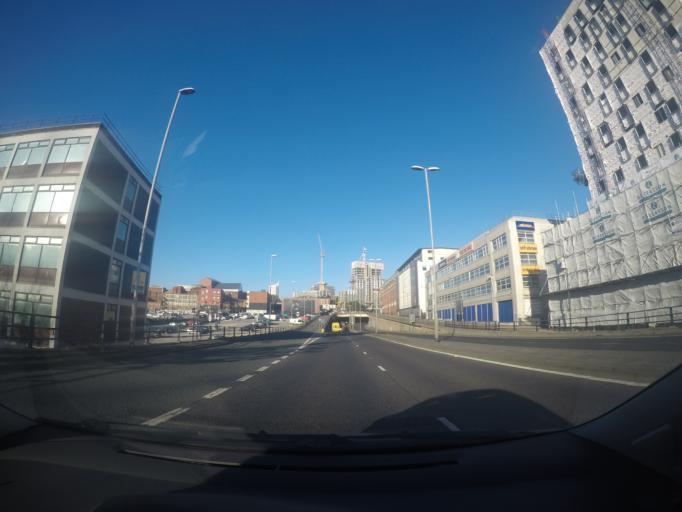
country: GB
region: England
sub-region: City and Borough of Leeds
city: Leeds
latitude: 53.8001
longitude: -1.5358
